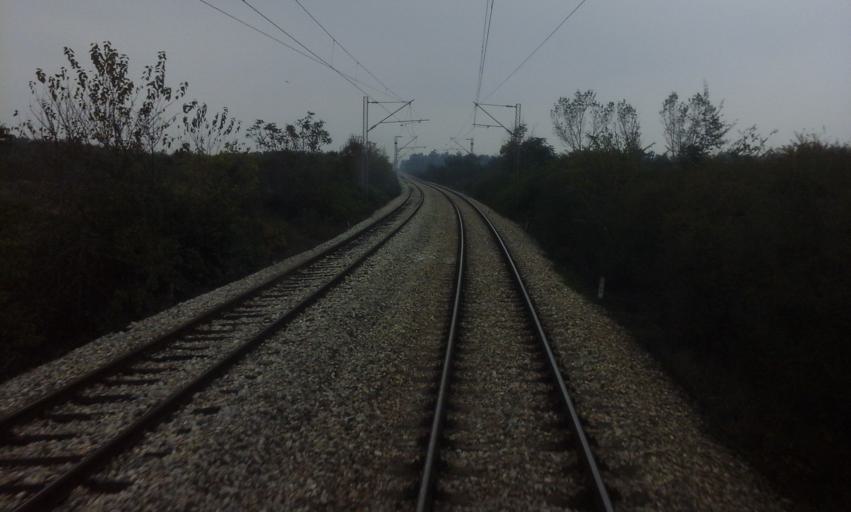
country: RS
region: Central Serbia
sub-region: Podunavski Okrug
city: Velika Plana
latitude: 44.2775
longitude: 21.0899
